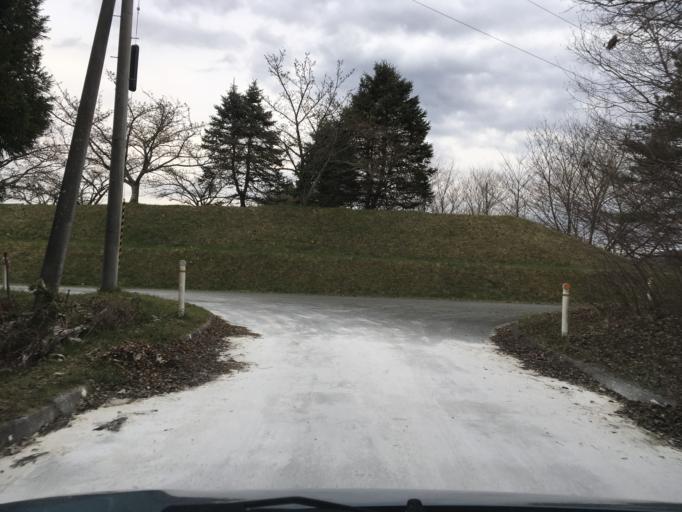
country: JP
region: Iwate
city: Ichinoseki
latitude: 38.8215
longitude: 141.2645
